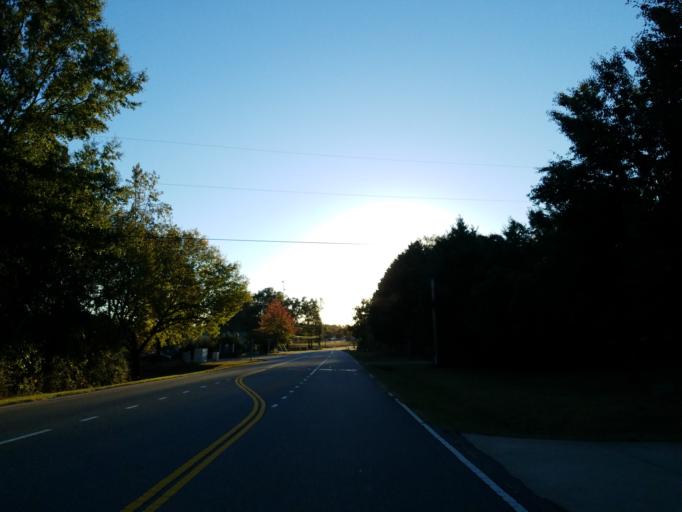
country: US
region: Georgia
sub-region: Forsyth County
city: Cumming
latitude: 34.2733
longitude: -84.0884
